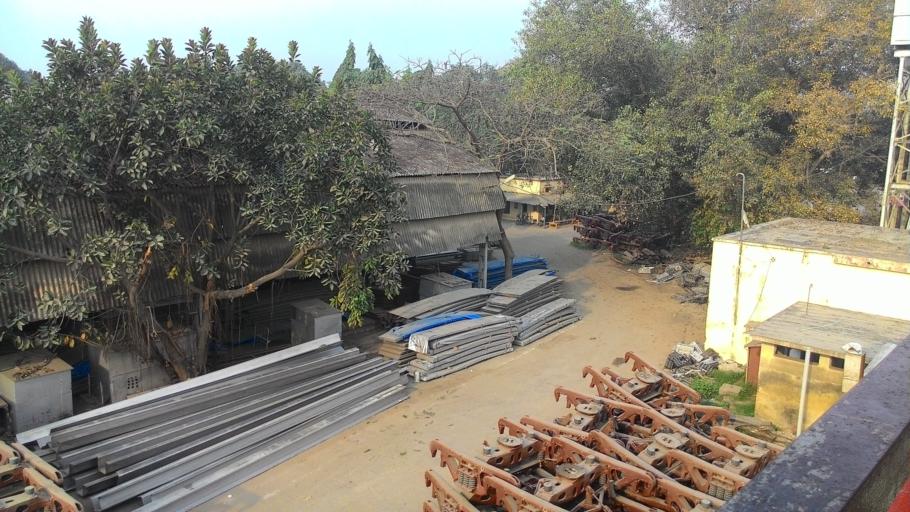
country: IN
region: Bihar
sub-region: Samastipur
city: Samastipur
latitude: 25.8558
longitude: 85.7864
